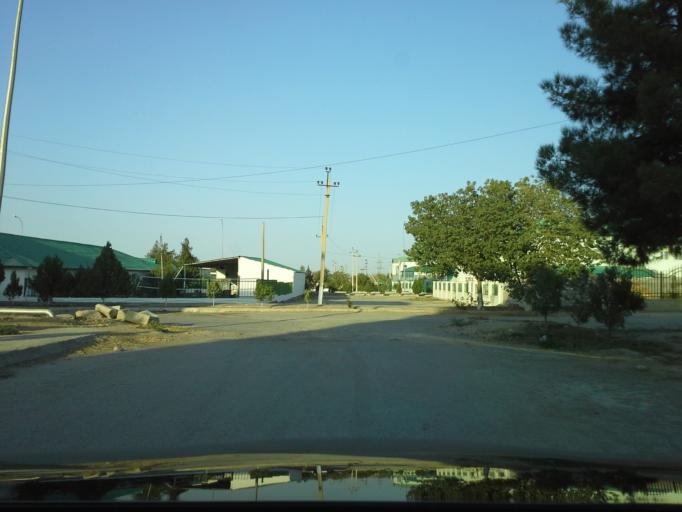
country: TM
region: Ahal
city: Abadan
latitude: 38.0357
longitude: 58.1919
